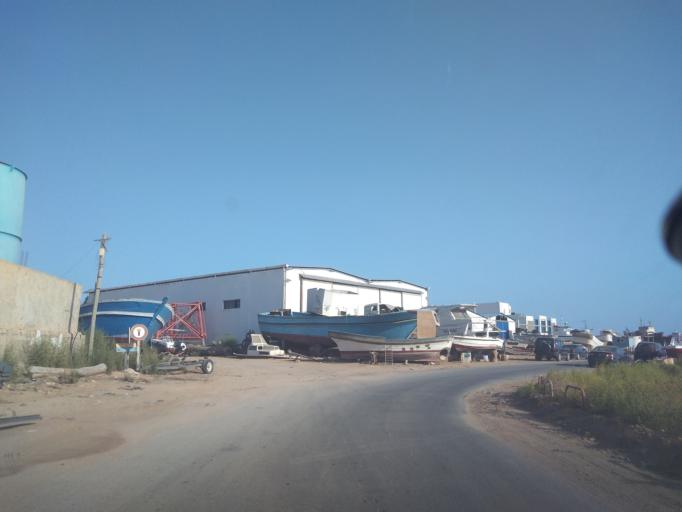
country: TN
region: Safaqis
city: Sfax
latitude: 34.7202
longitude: 10.7673
